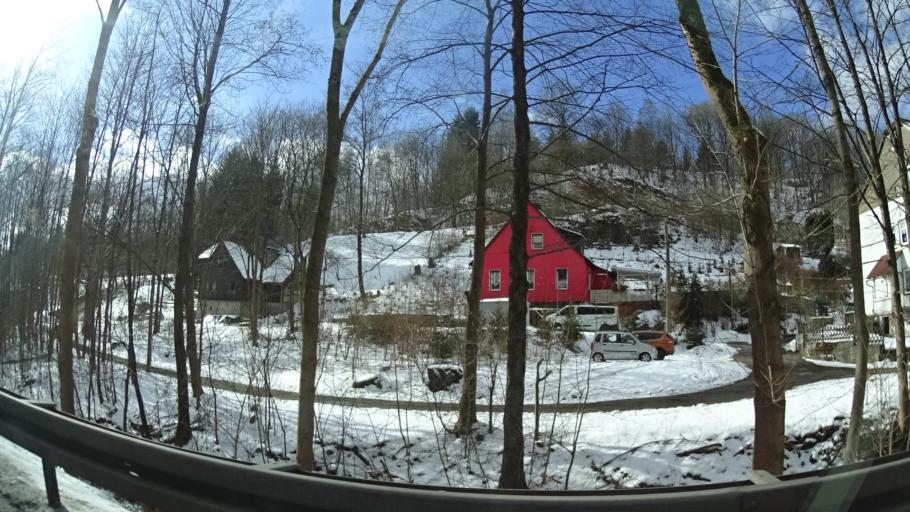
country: DE
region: Thuringia
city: Suhl
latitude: 50.6236
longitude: 10.6989
